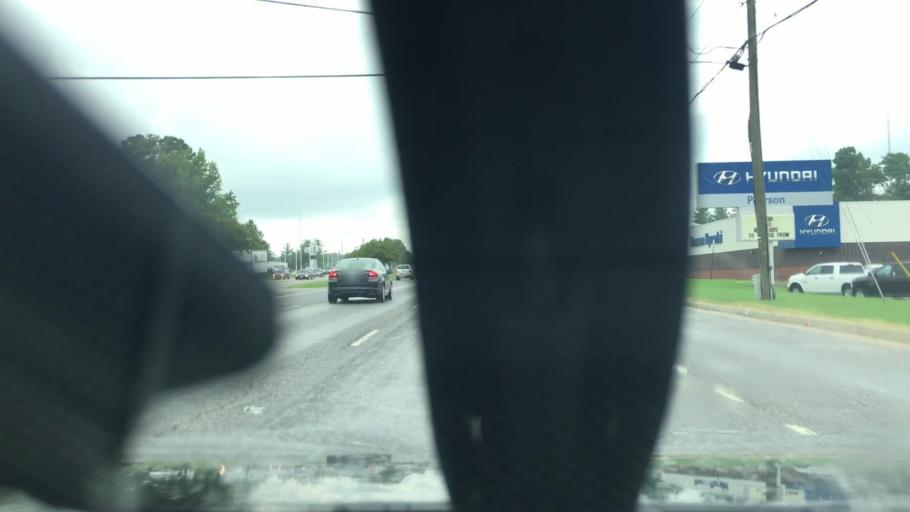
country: US
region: Virginia
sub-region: Chesterfield County
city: Bon Air
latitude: 37.5006
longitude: -77.5718
